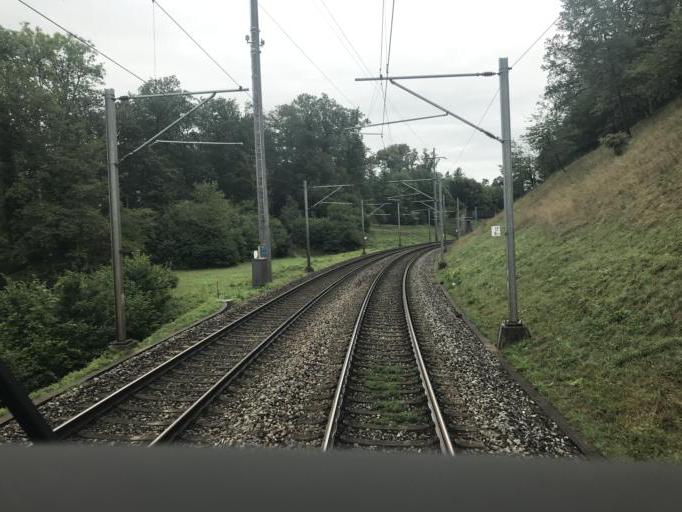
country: CH
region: Zurich
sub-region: Bezirk Buelach
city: Hochfelden
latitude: 47.5359
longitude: 8.5237
